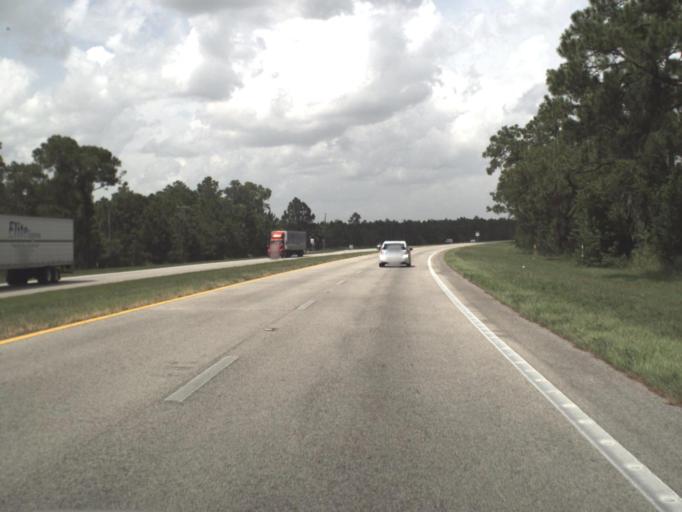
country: US
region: Florida
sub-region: Polk County
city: Crooked Lake Park
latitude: 27.7665
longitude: -81.5954
